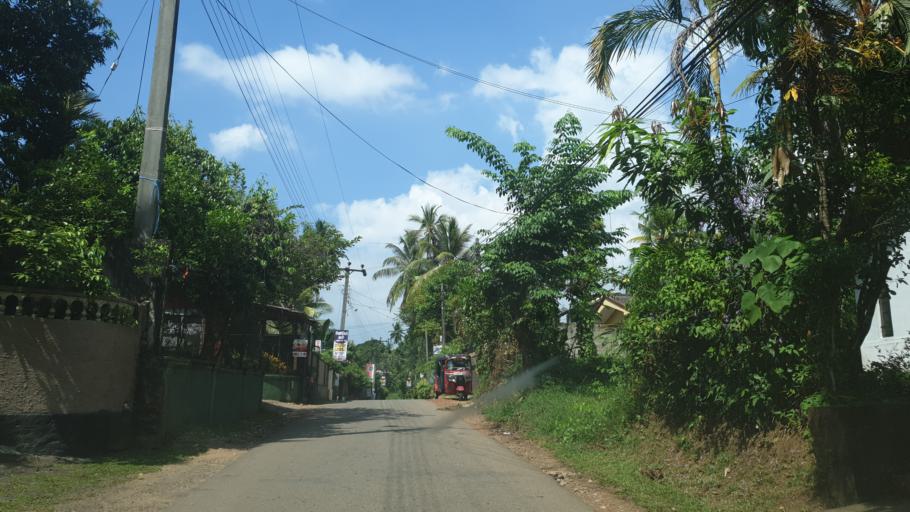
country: LK
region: Western
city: Horana South
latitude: 6.7077
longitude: 79.9836
